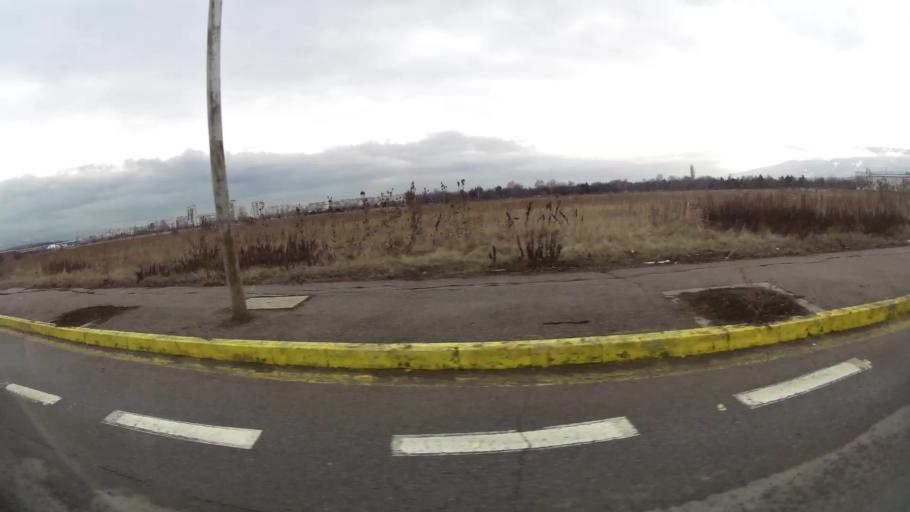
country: BG
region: Sofia-Capital
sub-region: Stolichna Obshtina
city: Sofia
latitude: 42.7376
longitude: 23.2731
